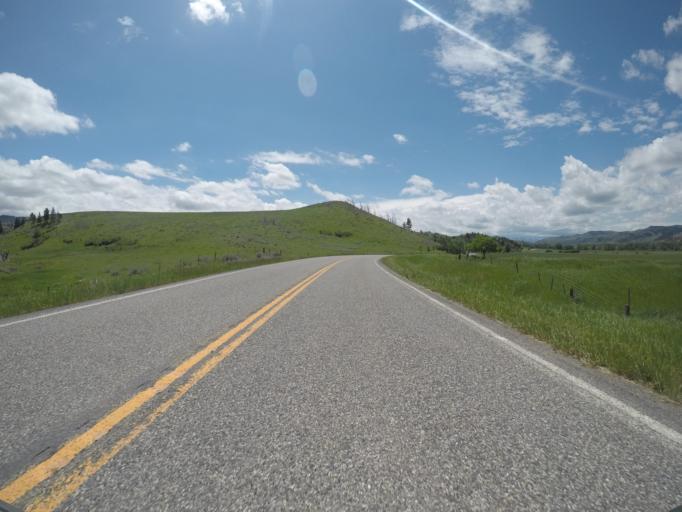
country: US
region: Montana
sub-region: Sweet Grass County
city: Big Timber
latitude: 45.6997
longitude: -110.0186
